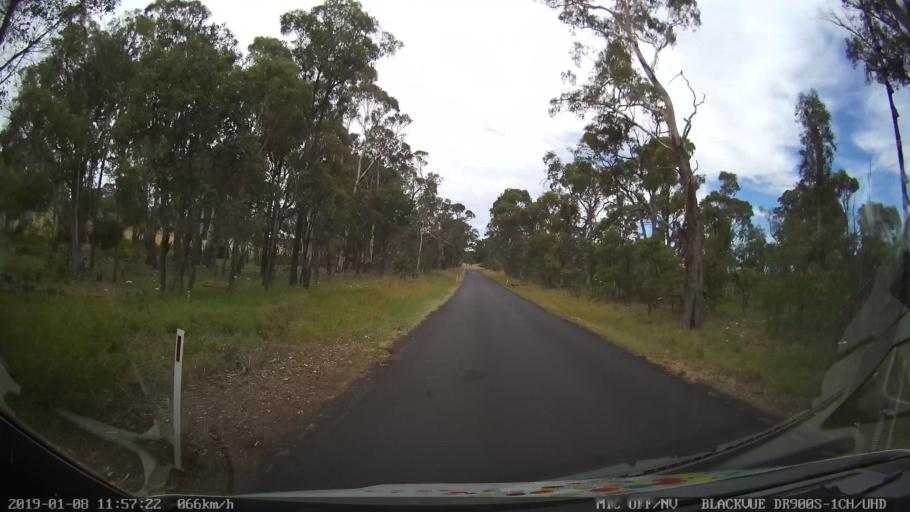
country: AU
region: New South Wales
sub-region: Armidale Dumaresq
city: Armidale
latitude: -30.4494
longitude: 151.5667
